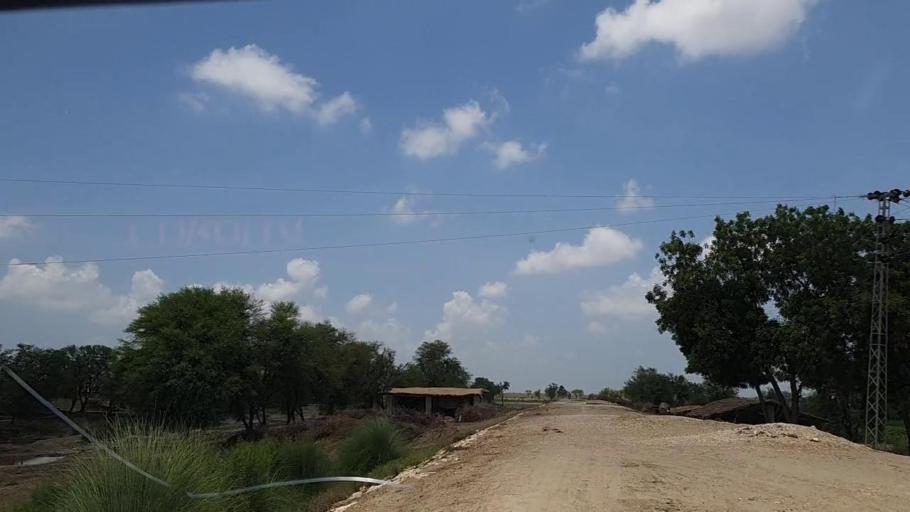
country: PK
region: Sindh
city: Tharu Shah
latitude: 26.9283
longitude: 67.9900
